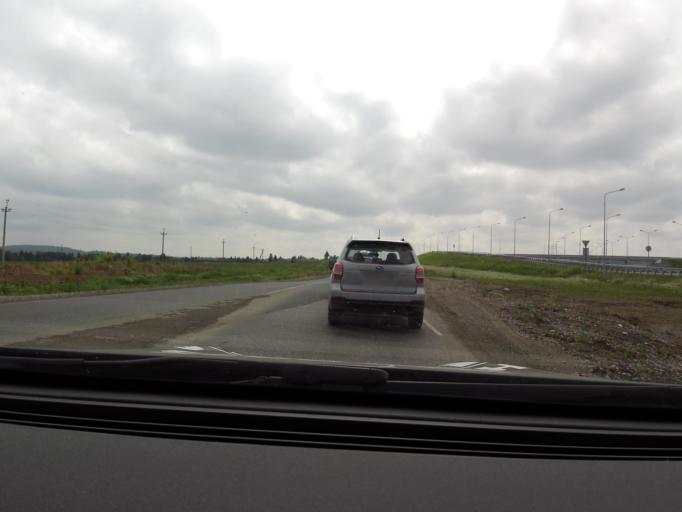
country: RU
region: Perm
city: Zvezdnyy
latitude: 57.7852
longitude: 56.3417
